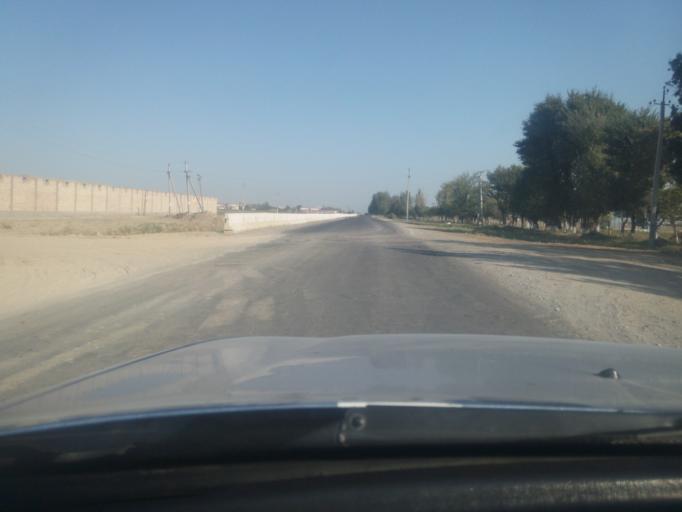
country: UZ
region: Sirdaryo
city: Guliston
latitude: 40.5049
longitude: 68.7971
